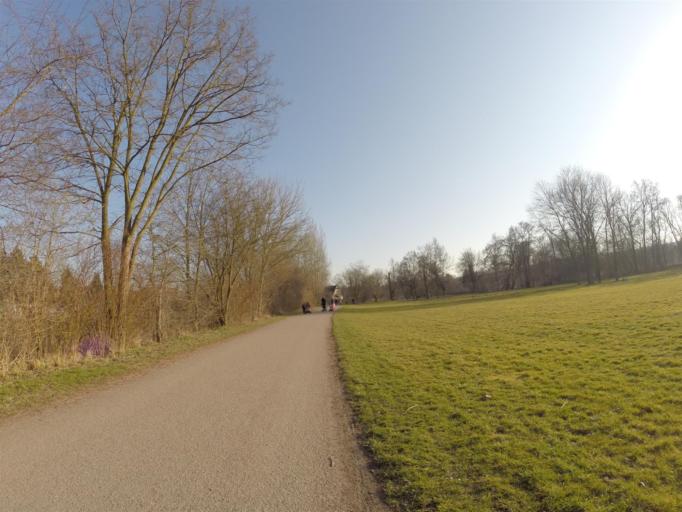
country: DE
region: Thuringia
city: Weimar
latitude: 50.9675
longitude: 11.3416
